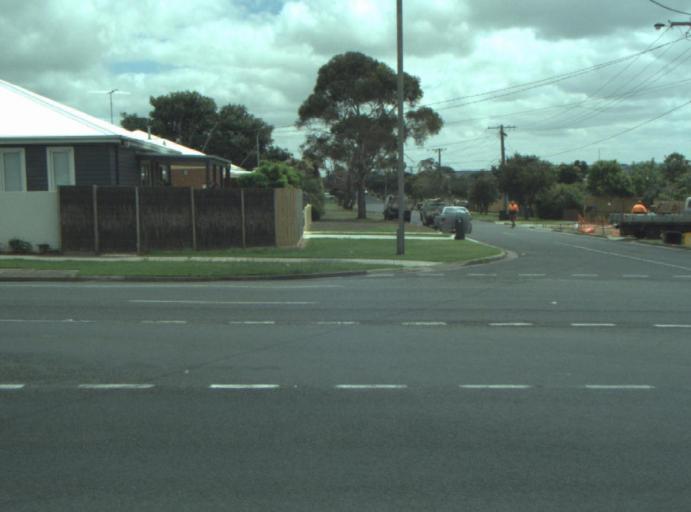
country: AU
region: Victoria
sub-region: Greater Geelong
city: Breakwater
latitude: -38.2050
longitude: 144.3407
